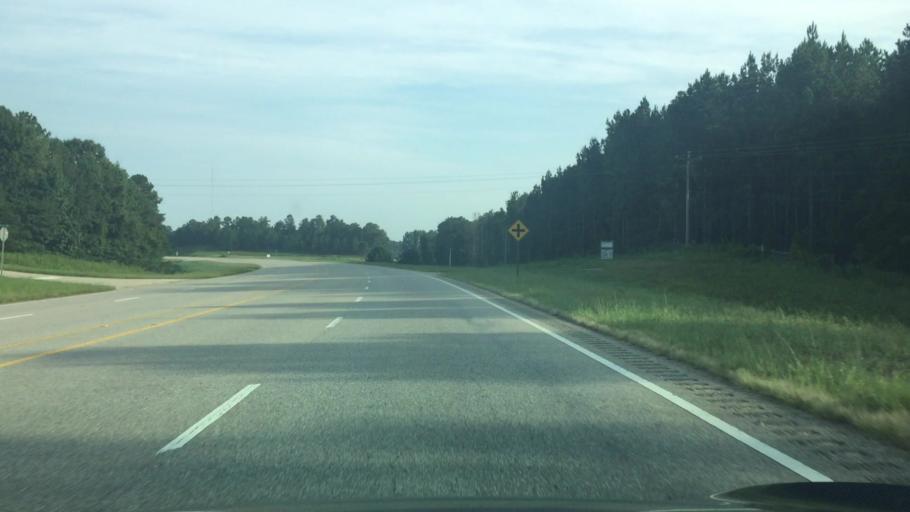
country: US
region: Alabama
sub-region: Covington County
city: Andalusia
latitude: 31.4401
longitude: -86.6120
